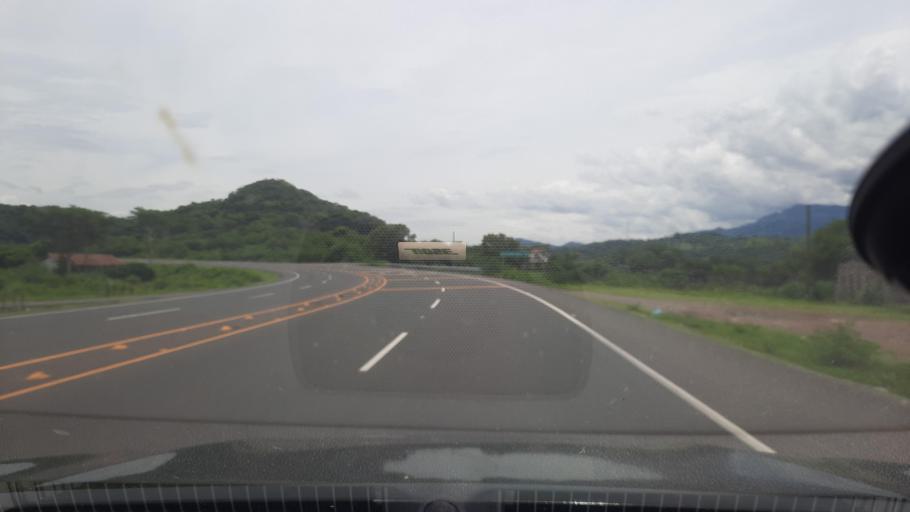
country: HN
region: Valle
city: Aramecina
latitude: 13.7247
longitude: -87.7098
